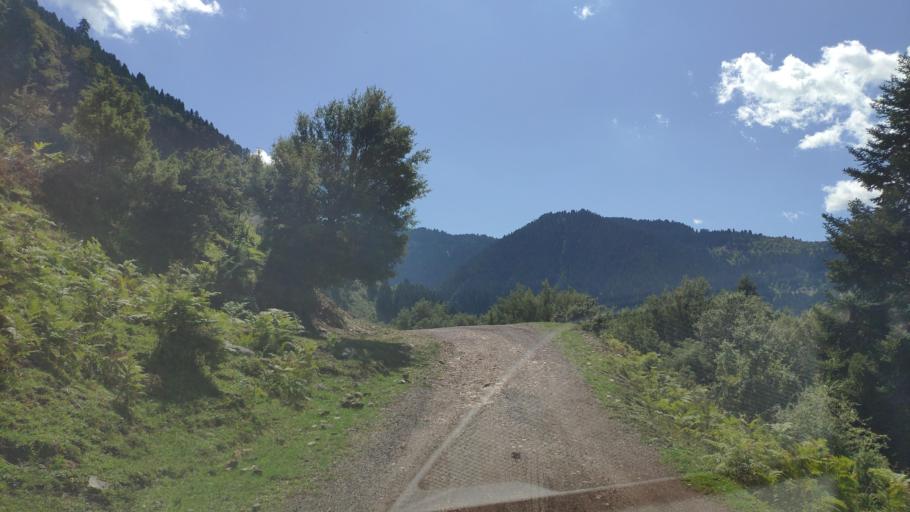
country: GR
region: Central Greece
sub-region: Nomos Evrytanias
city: Kerasochori
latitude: 39.1347
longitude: 21.6568
